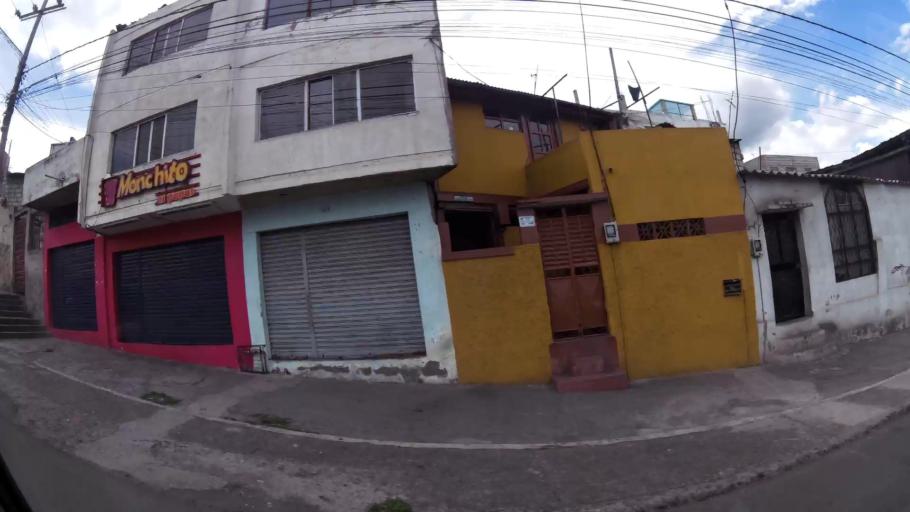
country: EC
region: Tungurahua
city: Ambato
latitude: -1.2506
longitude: -78.6223
